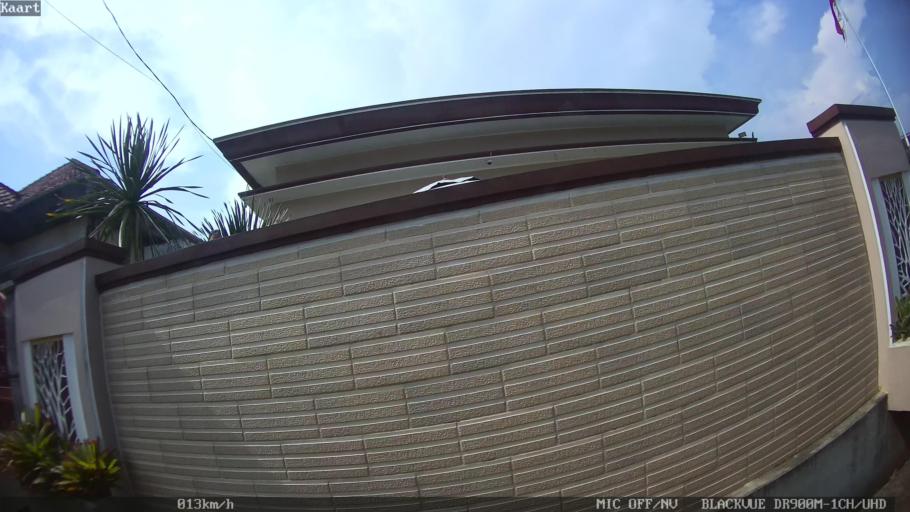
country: ID
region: Lampung
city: Kedaton
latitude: -5.3991
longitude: 105.2277
